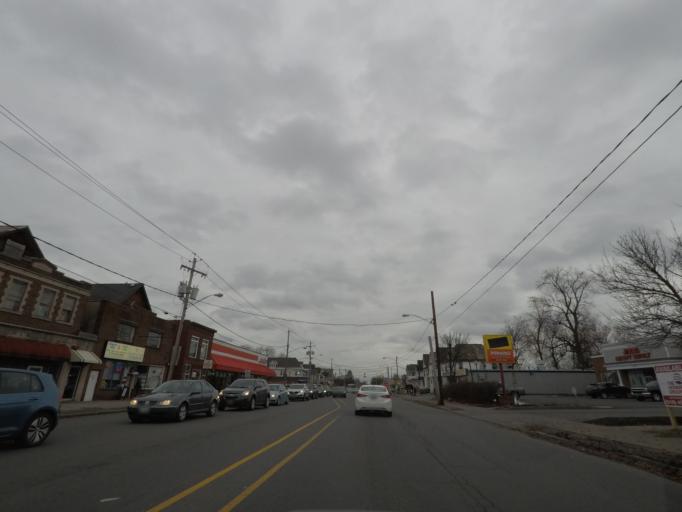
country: US
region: New York
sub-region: Schenectady County
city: Schenectady
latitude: 42.8006
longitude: -73.9270
